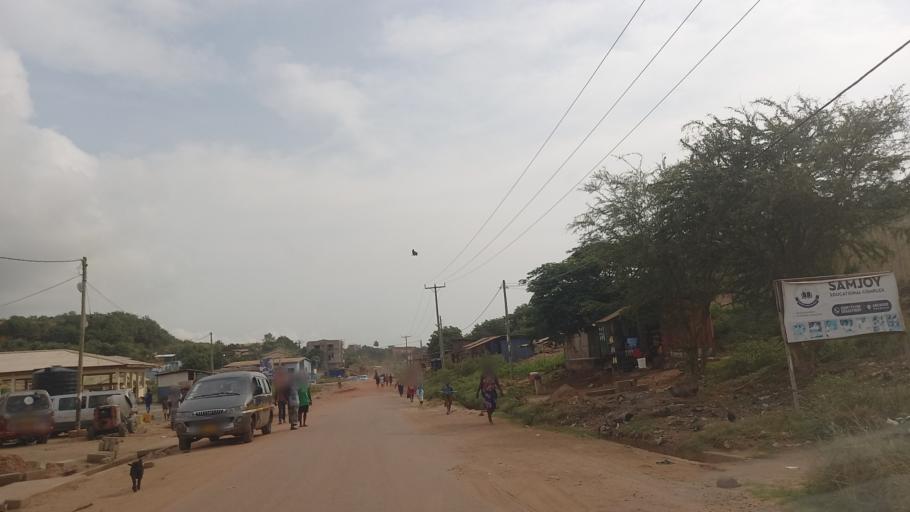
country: GH
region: Western
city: Shama Junction
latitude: 4.9754
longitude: -1.6487
